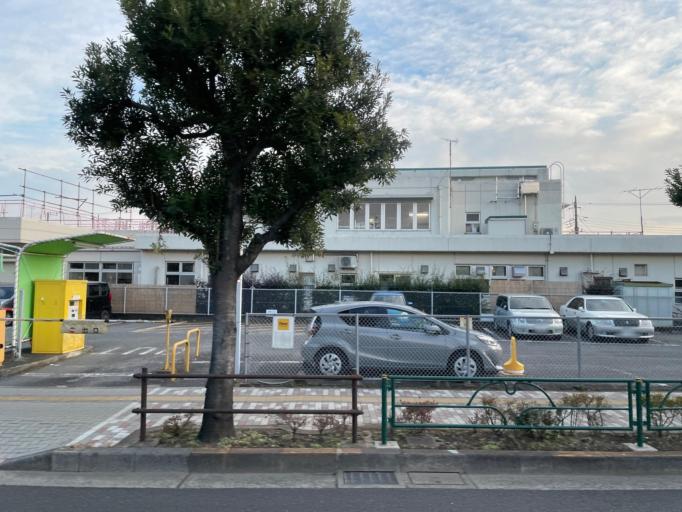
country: JP
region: Tokyo
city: Tanashicho
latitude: 35.7571
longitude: 139.5267
